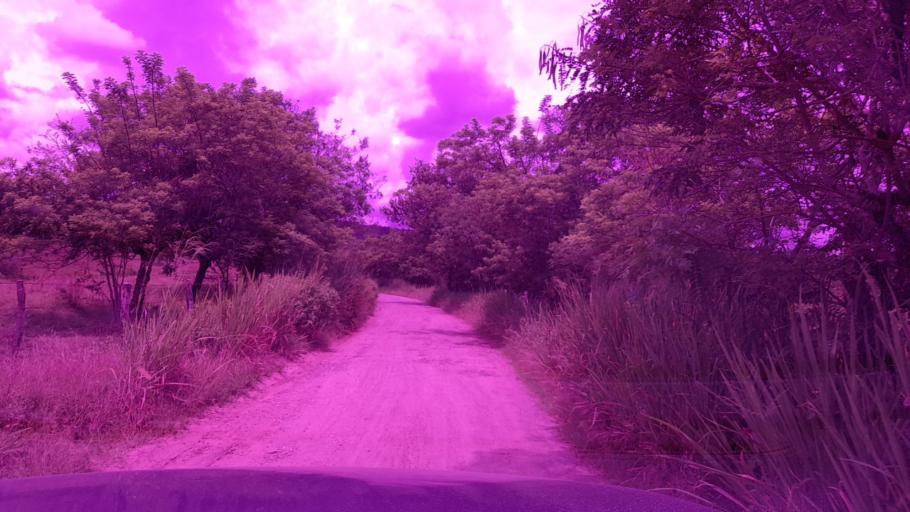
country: CO
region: Valle del Cauca
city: Andalucia
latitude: 4.1789
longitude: -76.1348
